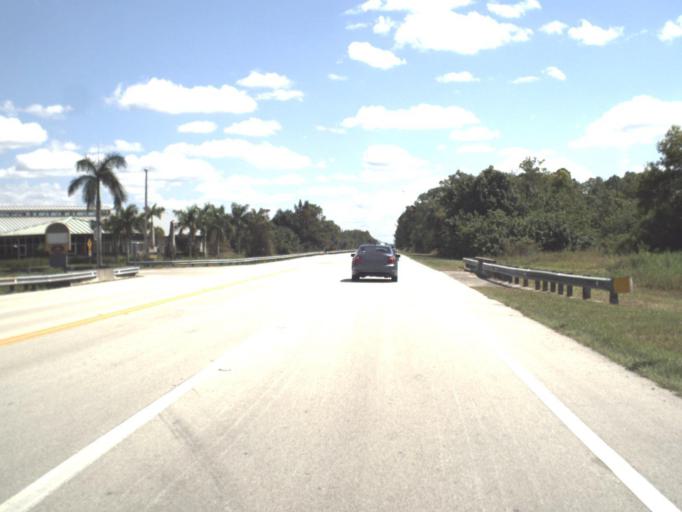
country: US
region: Florida
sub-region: Collier County
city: Lely Resort
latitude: 26.0257
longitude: -81.6405
